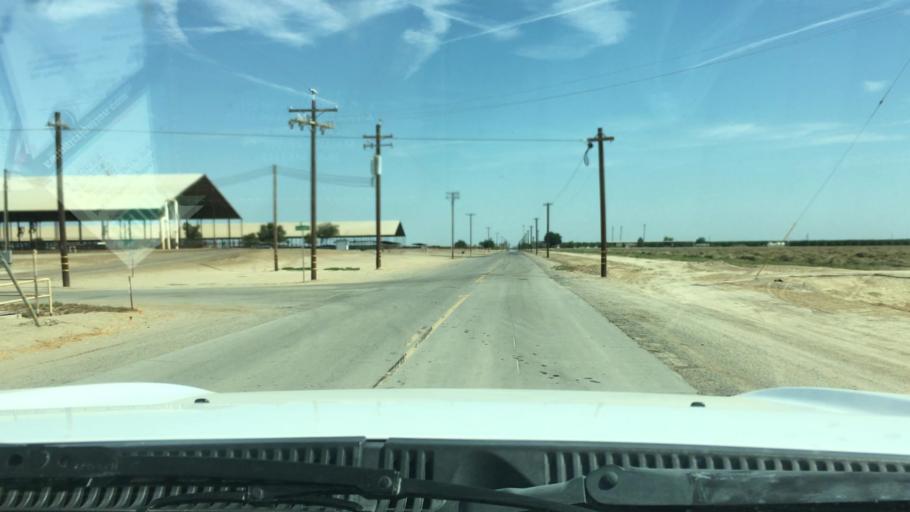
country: US
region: California
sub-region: Kern County
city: Buttonwillow
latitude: 35.4129
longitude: -119.3765
